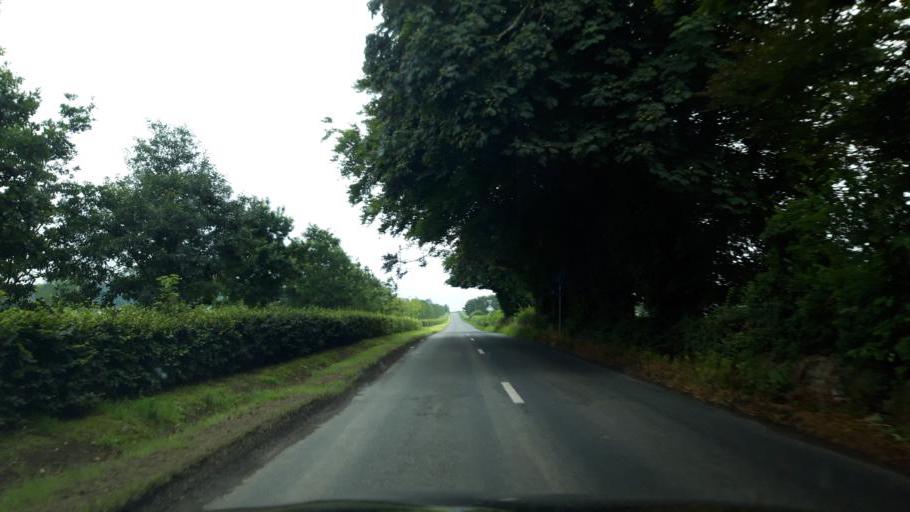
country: IE
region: Munster
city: Fethard
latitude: 52.4915
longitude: -7.6907
